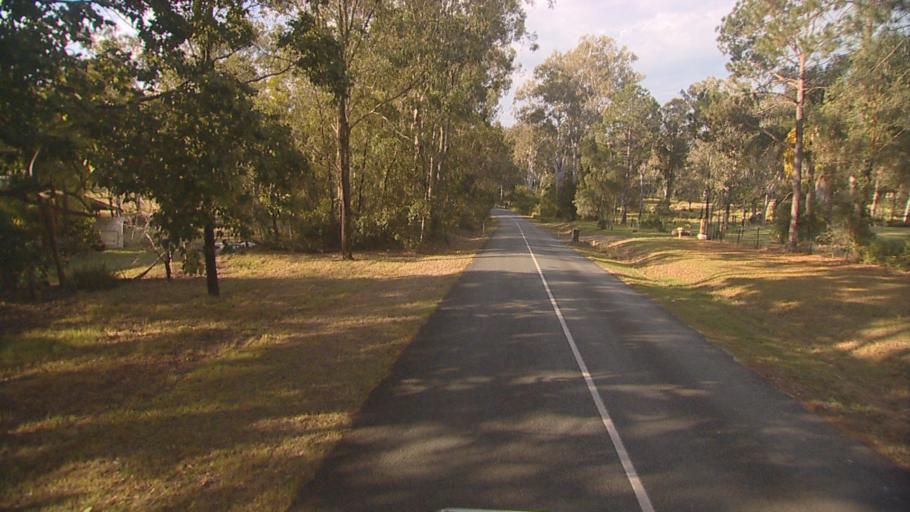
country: AU
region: Queensland
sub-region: Gold Coast
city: Ormeau Hills
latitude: -27.8443
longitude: 153.1546
